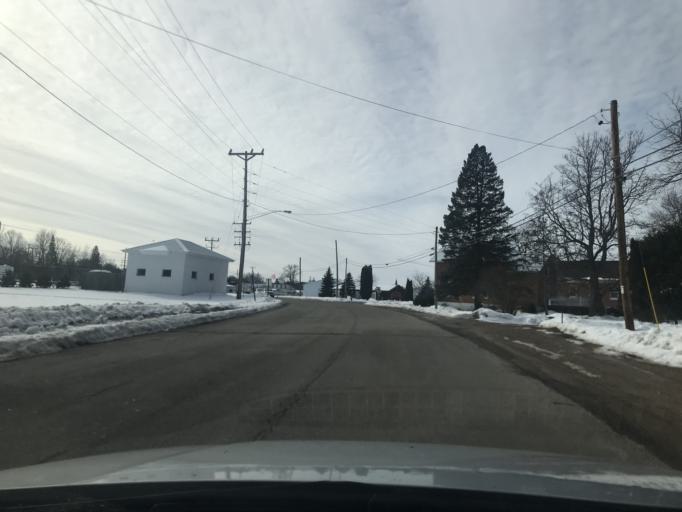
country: US
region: Wisconsin
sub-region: Oconto County
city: Gillett
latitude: 44.8935
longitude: -88.3009
